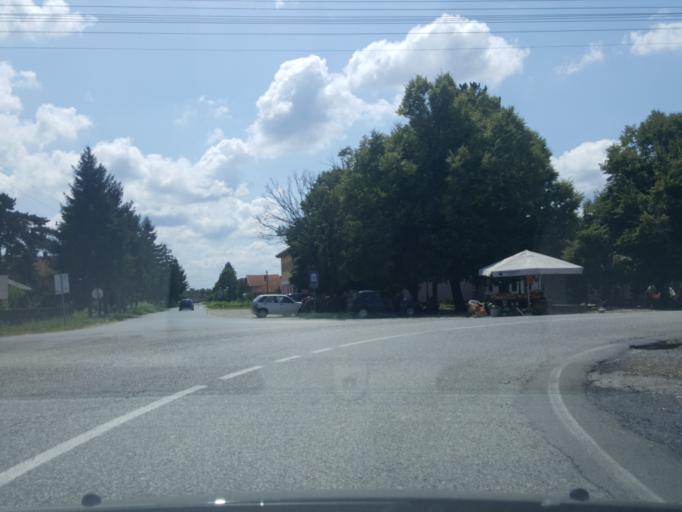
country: RS
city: Metkovic
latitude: 44.8554
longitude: 19.5461
